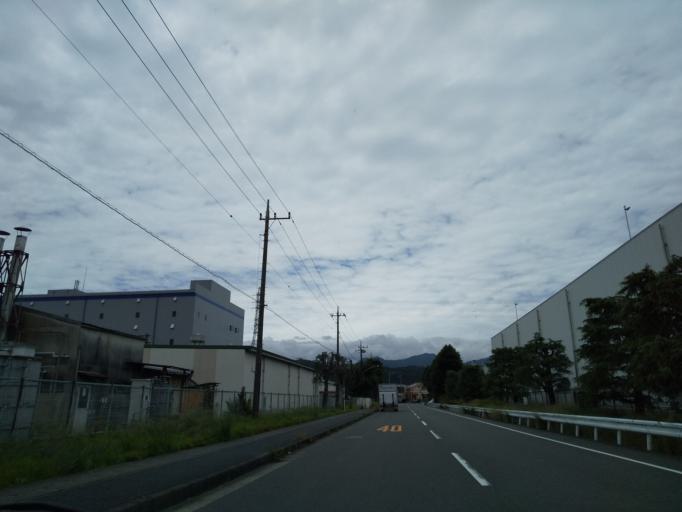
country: JP
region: Kanagawa
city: Zama
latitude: 35.5128
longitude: 139.3437
